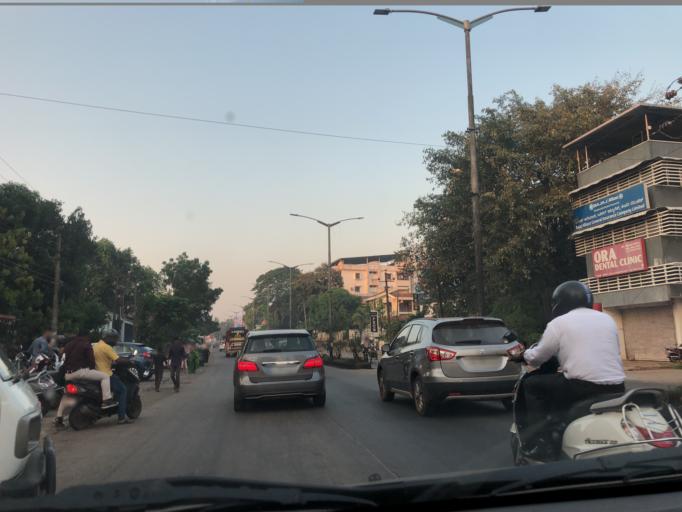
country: IN
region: Karnataka
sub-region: Dakshina Kannada
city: Mangalore
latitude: 12.8915
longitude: 74.8356
